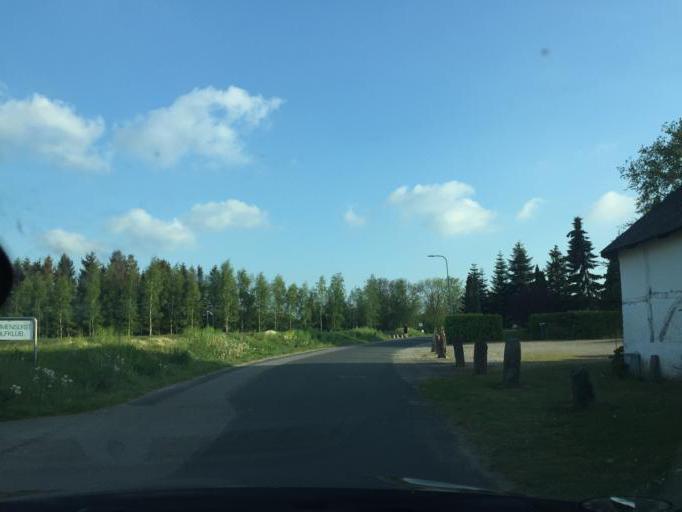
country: DK
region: South Denmark
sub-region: Odense Kommune
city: Bellinge
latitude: 55.3882
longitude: 10.2808
